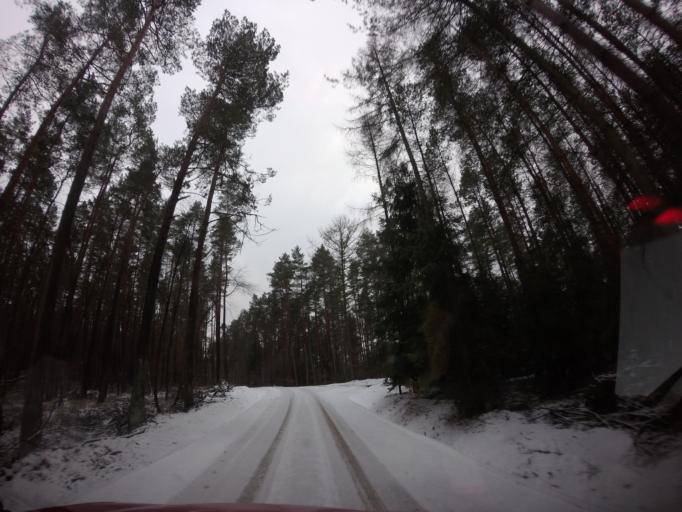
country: PL
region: West Pomeranian Voivodeship
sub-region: Powiat choszczenski
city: Pelczyce
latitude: 52.9604
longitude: 15.3555
